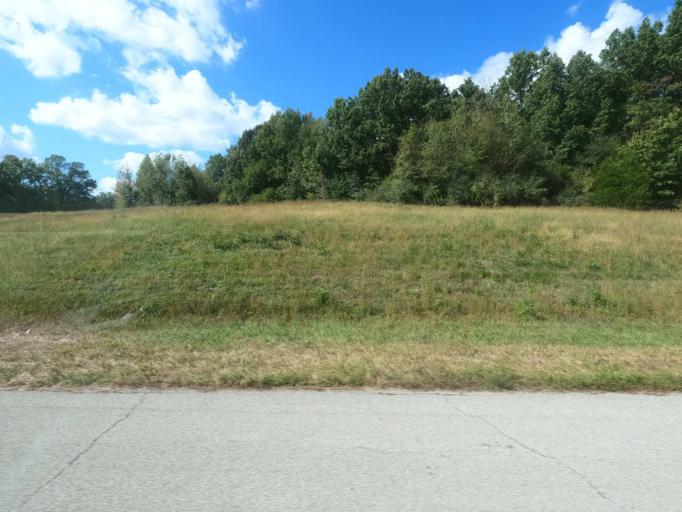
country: US
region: Illinois
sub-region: Johnson County
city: Vienna
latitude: 37.4434
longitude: -88.8909
